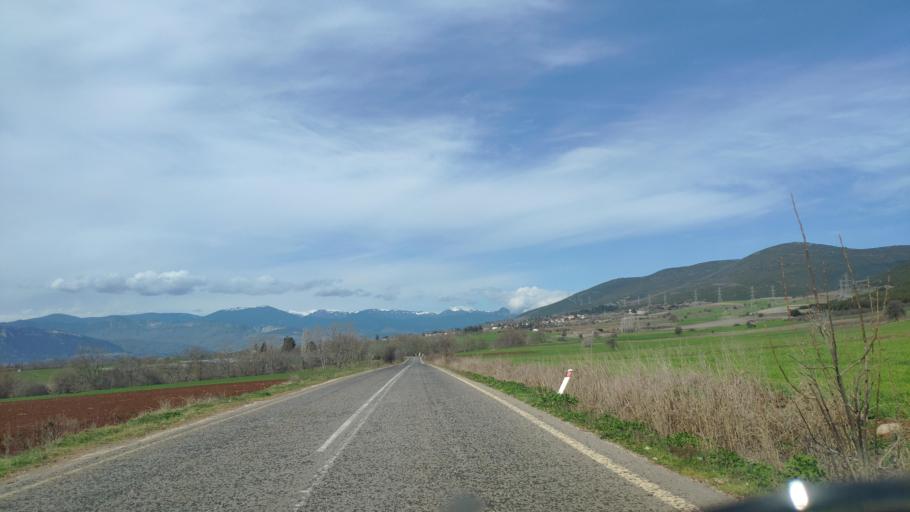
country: GR
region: Central Greece
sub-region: Nomos Fthiotidos
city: Amfikleia
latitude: 38.7040
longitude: 22.5068
